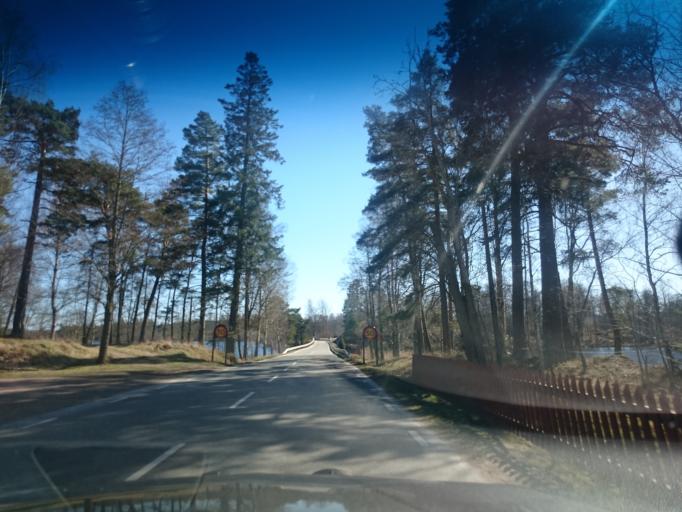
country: SE
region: Kronoberg
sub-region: Vaxjo Kommun
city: Braas
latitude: 57.1996
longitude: 14.9580
